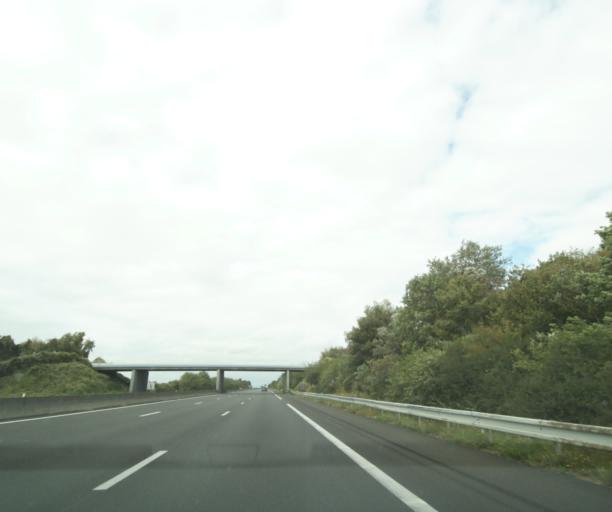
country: FR
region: Centre
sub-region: Departement d'Eure-et-Loir
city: Janville
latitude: 48.2311
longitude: 1.8489
